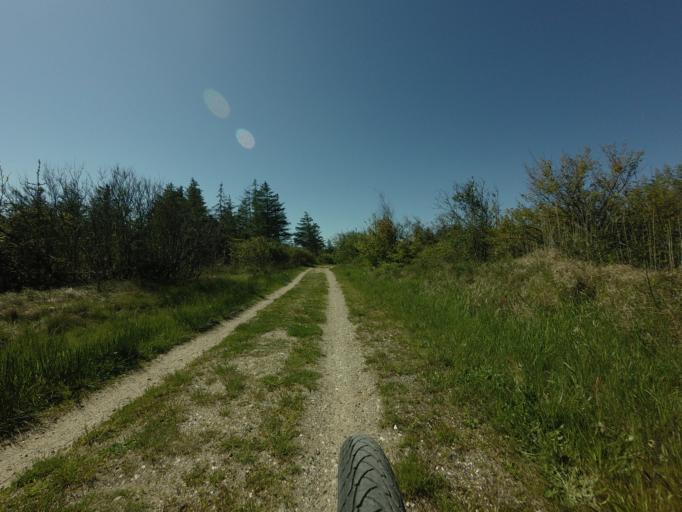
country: DK
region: North Denmark
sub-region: Jammerbugt Kommune
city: Pandrup
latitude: 57.2805
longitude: 9.6351
